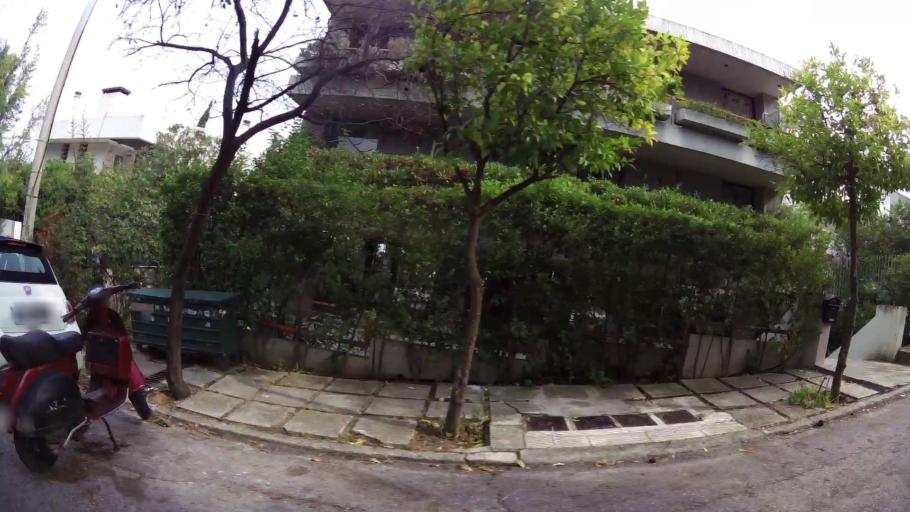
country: GR
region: Attica
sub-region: Nomarchia Athinas
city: Filothei
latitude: 38.0266
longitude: 23.7734
